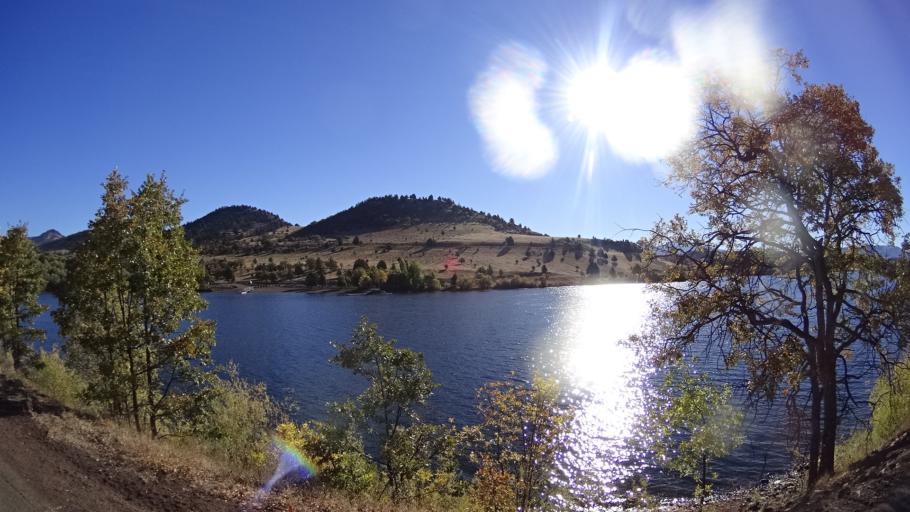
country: US
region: California
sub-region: Siskiyou County
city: Montague
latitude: 41.9720
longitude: -122.4391
